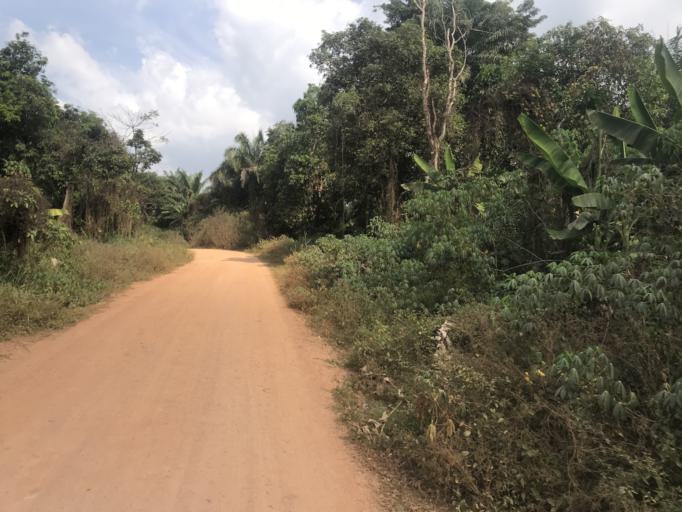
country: NG
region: Osun
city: Inisa
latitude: 7.8812
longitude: 4.3891
